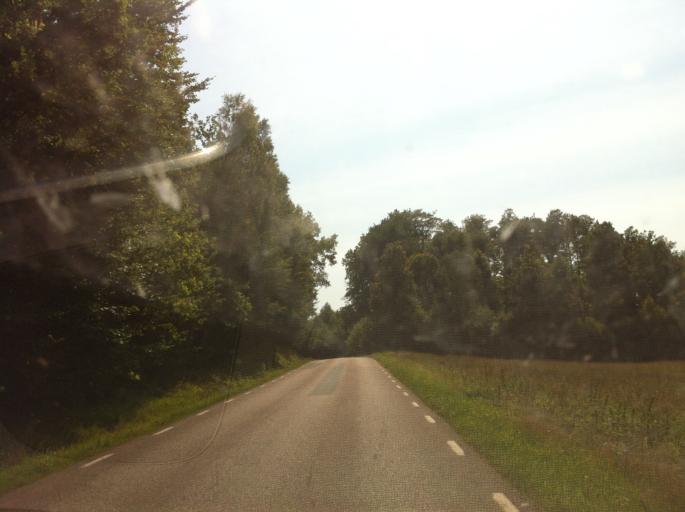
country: SE
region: Skane
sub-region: Hoors Kommun
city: Hoeoer
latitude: 56.0095
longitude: 13.4907
